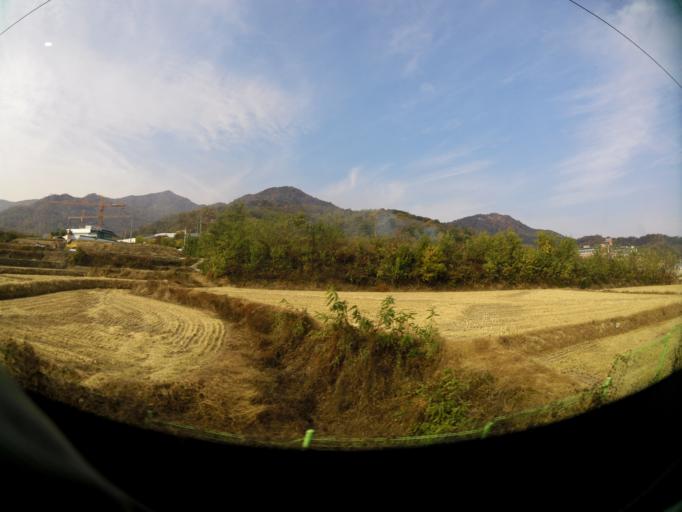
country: KR
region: Gyeongsangbuk-do
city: Gumi
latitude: 36.0938
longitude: 128.3538
